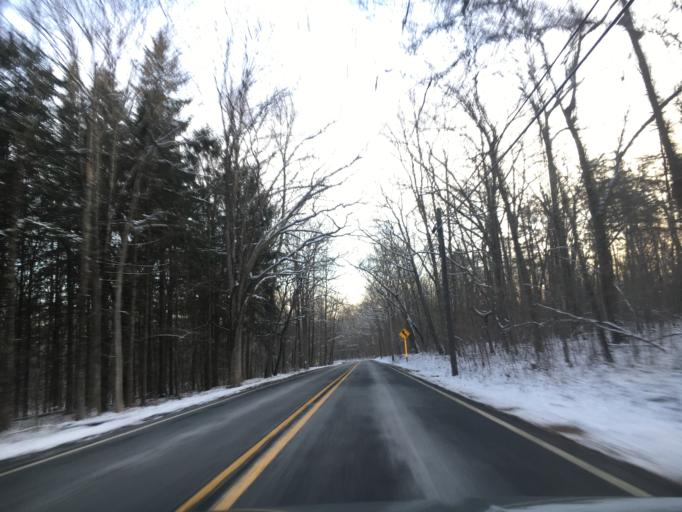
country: US
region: Pennsylvania
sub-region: Pike County
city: Saw Creek
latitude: 41.1626
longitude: -75.0837
